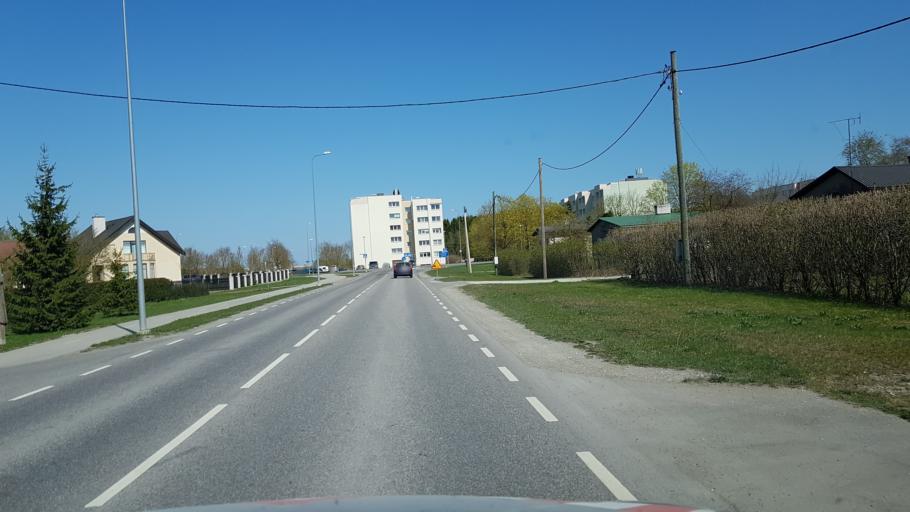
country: EE
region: Harju
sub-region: Joelaehtme vald
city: Loo
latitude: 59.4349
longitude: 24.9402
